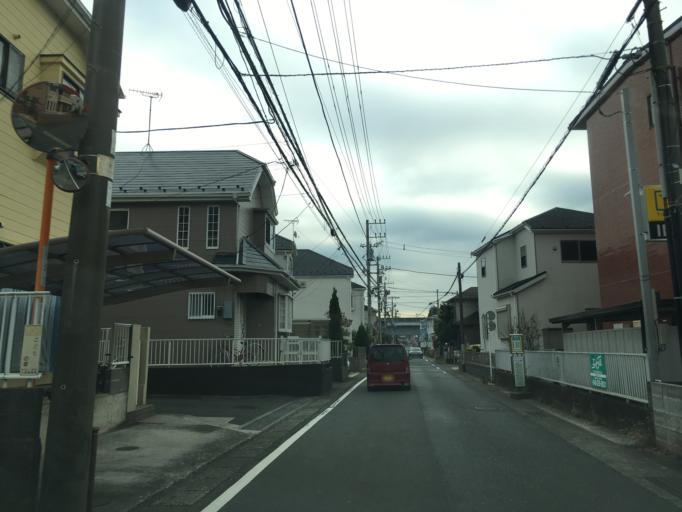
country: JP
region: Tokyo
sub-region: Machida-shi
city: Machida
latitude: 35.5126
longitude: 139.4636
